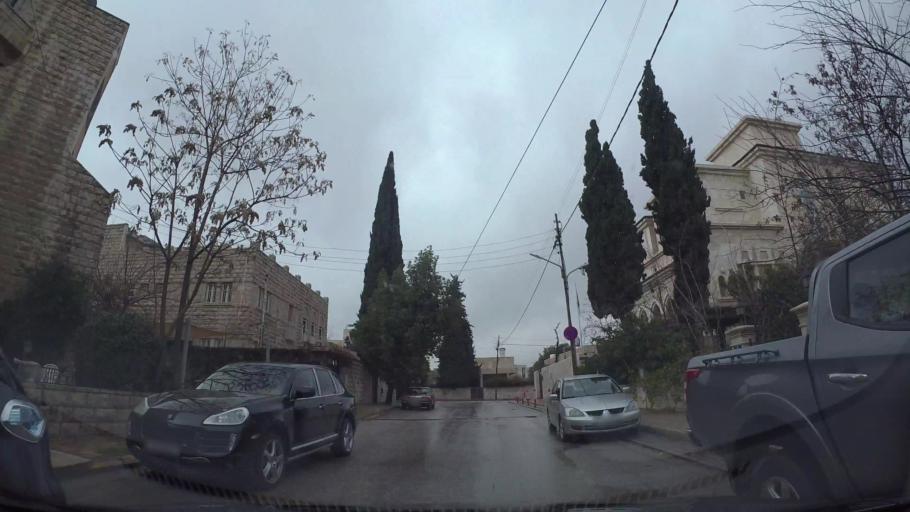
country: JO
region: Amman
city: Amman
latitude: 31.9570
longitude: 35.9045
